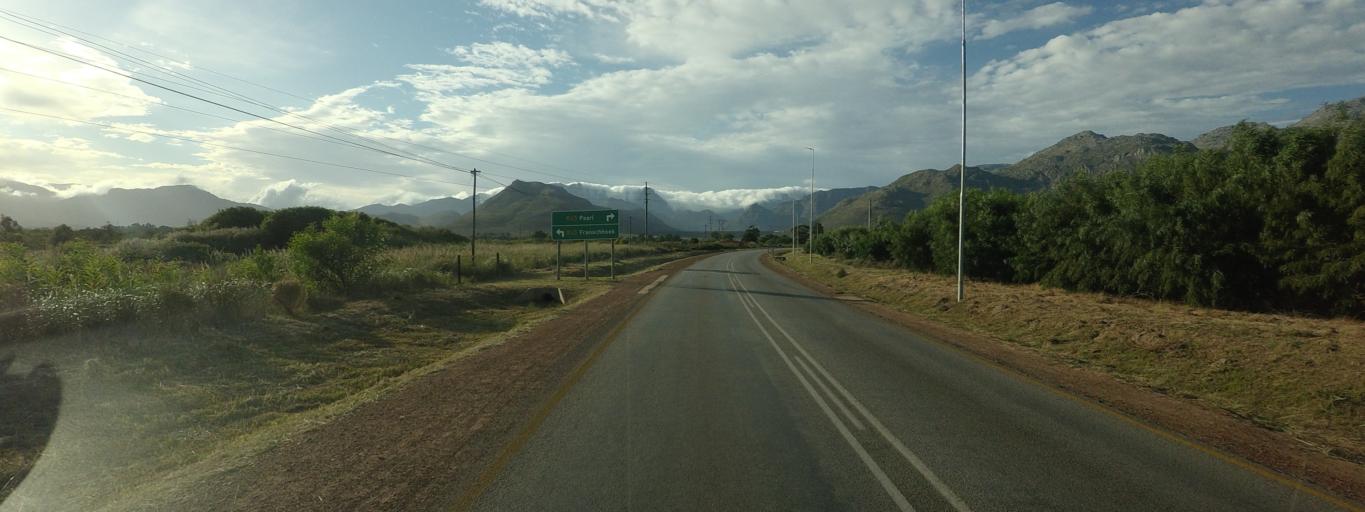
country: ZA
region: Western Cape
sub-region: Cape Winelands District Municipality
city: Paarl
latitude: -33.8725
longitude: 19.0443
